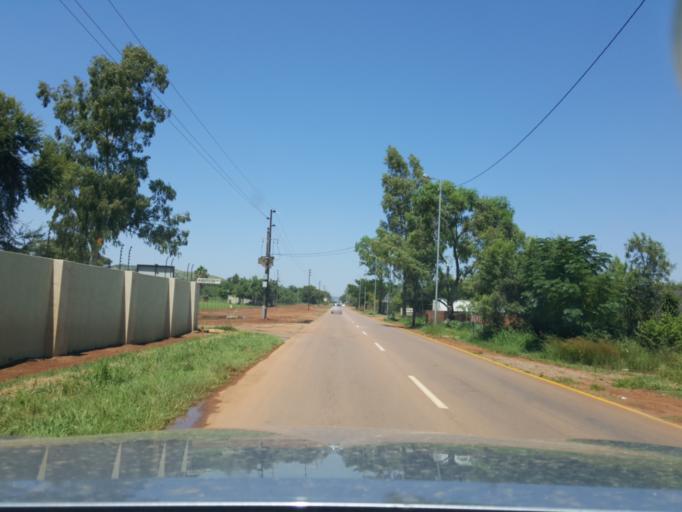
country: ZA
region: Gauteng
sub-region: City of Tshwane Metropolitan Municipality
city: Pretoria
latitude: -25.6697
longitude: 28.3053
